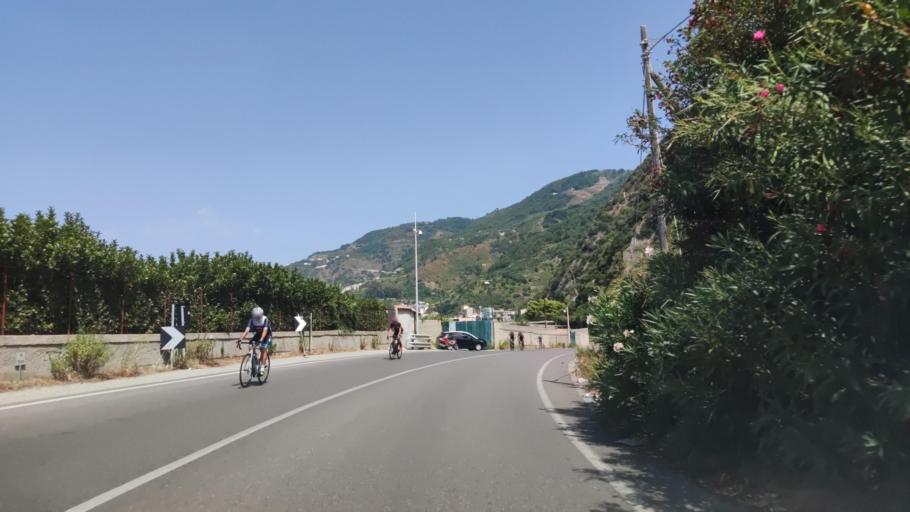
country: IT
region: Calabria
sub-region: Provincia di Reggio Calabria
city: Bagnara Calabra
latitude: 38.2789
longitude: 15.7909
